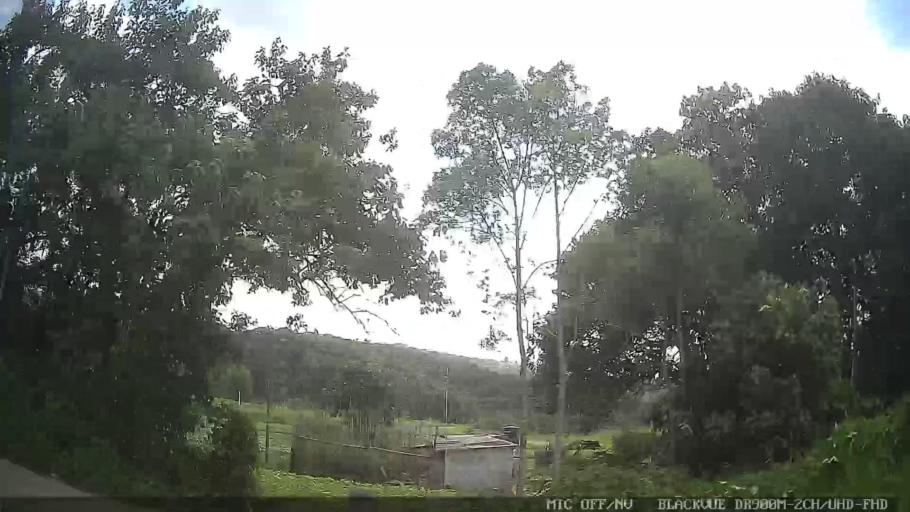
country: BR
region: Sao Paulo
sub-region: Ferraz De Vasconcelos
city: Ferraz de Vasconcelos
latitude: -23.5945
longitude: -46.3646
